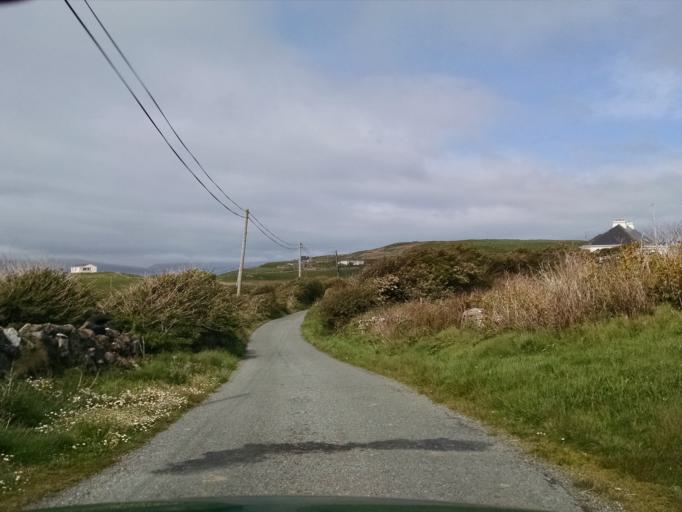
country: IE
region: Connaught
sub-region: County Galway
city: Clifden
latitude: 53.7595
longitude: -9.8821
